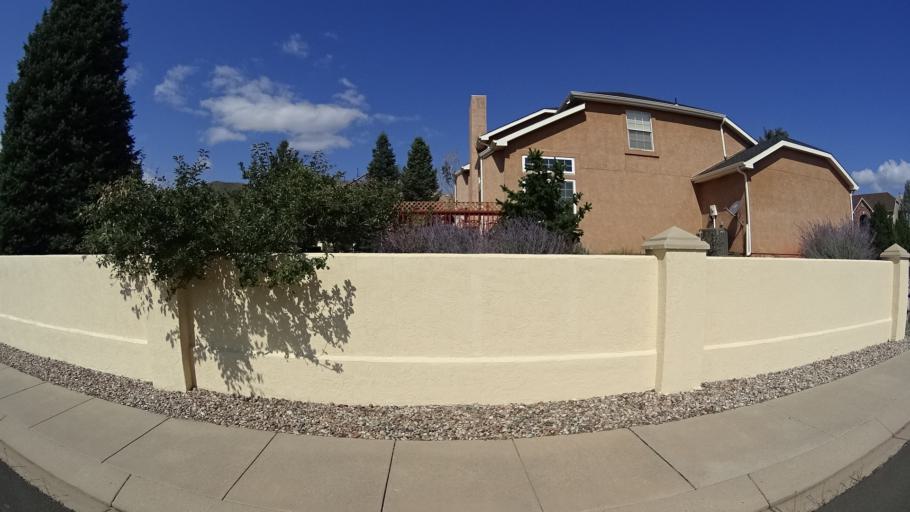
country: US
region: Colorado
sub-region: El Paso County
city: Manitou Springs
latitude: 38.9173
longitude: -104.8729
